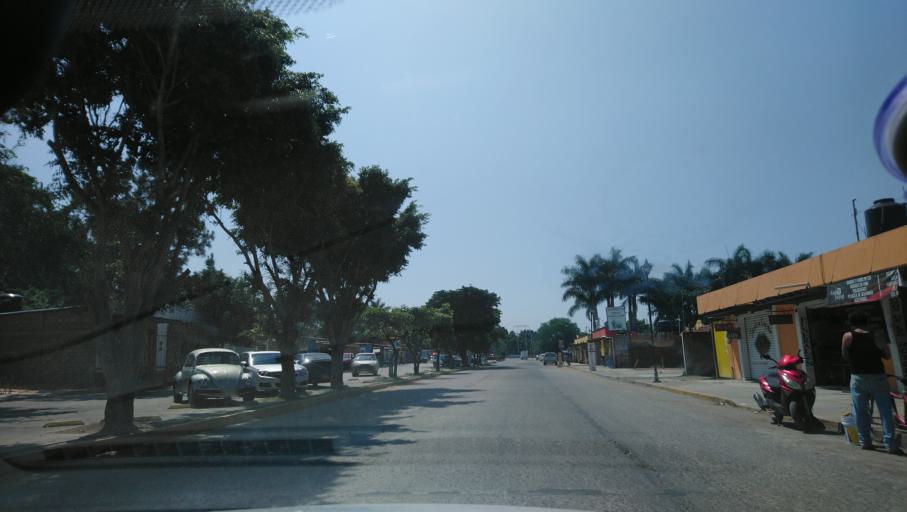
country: MX
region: Oaxaca
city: Santa Maria del Tule
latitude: 17.0450
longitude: -96.6354
